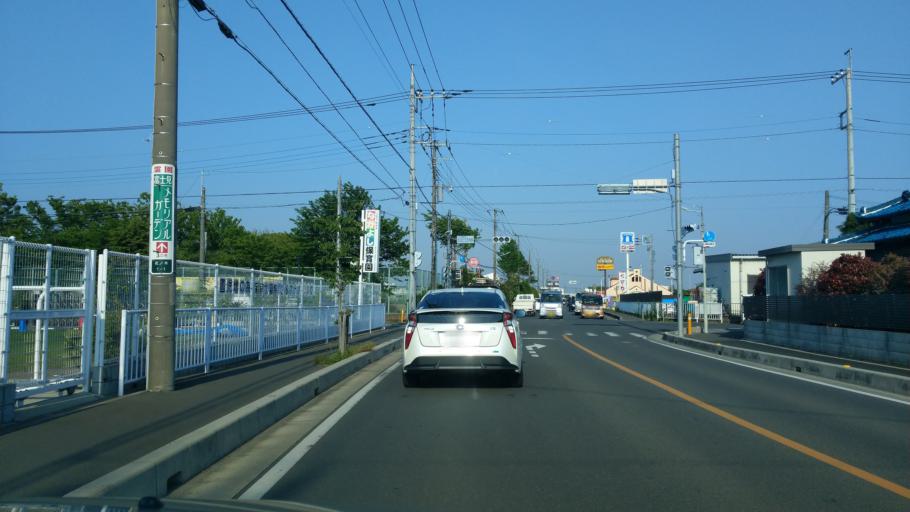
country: JP
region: Saitama
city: Kamifukuoka
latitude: 35.8758
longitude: 139.5337
